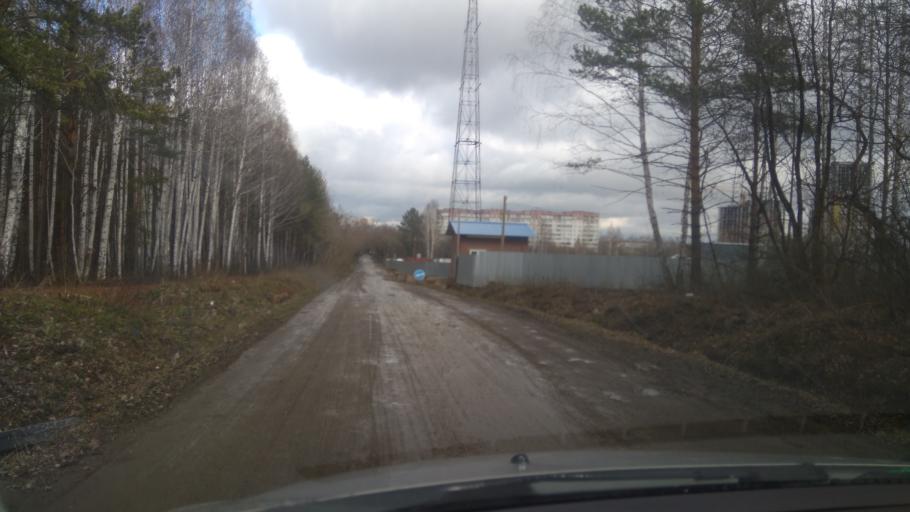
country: RU
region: Sverdlovsk
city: Verkhnyaya Pyshma
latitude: 56.9235
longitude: 60.6029
